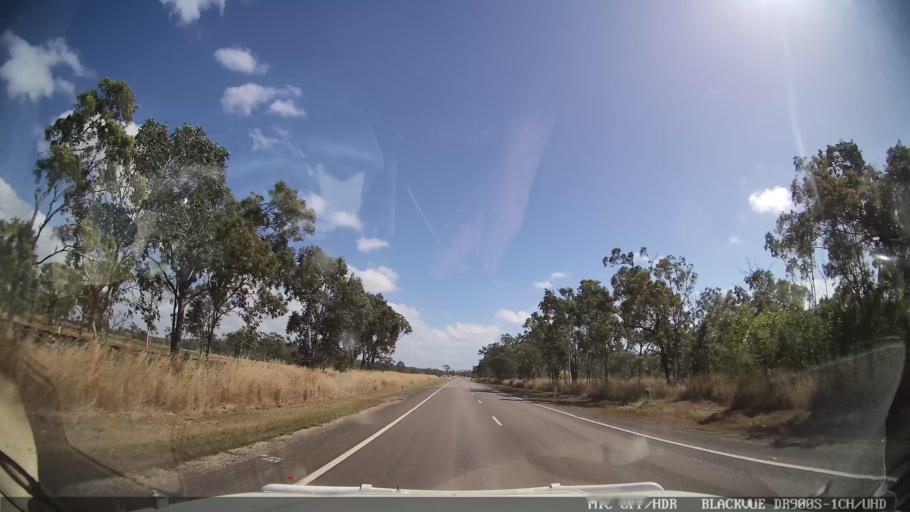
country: AU
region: Queensland
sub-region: Whitsunday
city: Red Hill
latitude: -20.1854
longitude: 148.3556
